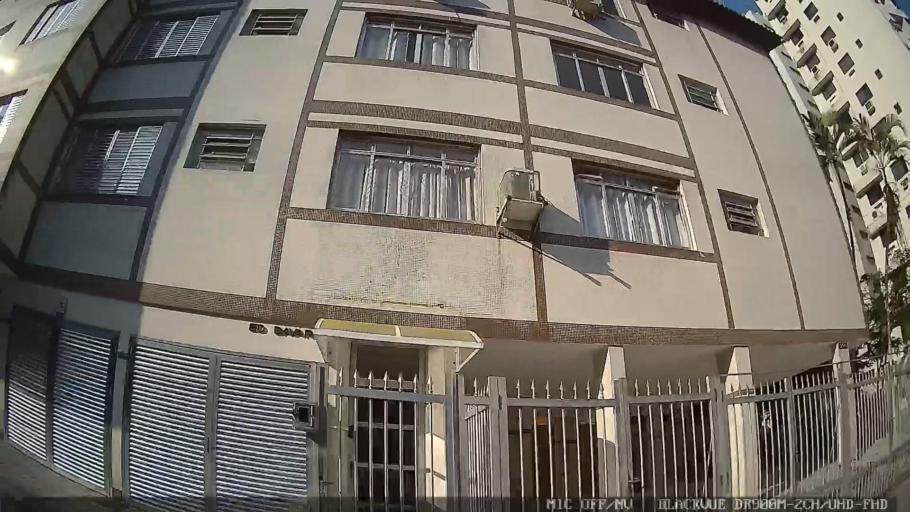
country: BR
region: Sao Paulo
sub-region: Guaruja
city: Guaruja
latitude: -23.9998
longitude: -46.2672
